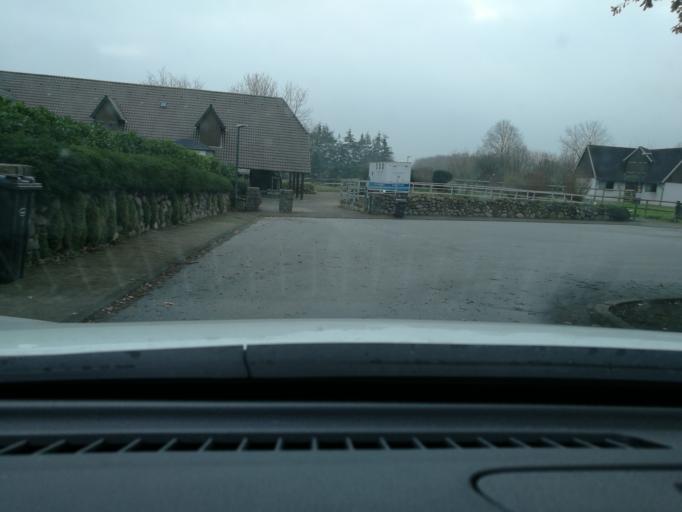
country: DE
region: Schleswig-Holstein
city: Holzbunge
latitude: 54.3818
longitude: 9.7074
